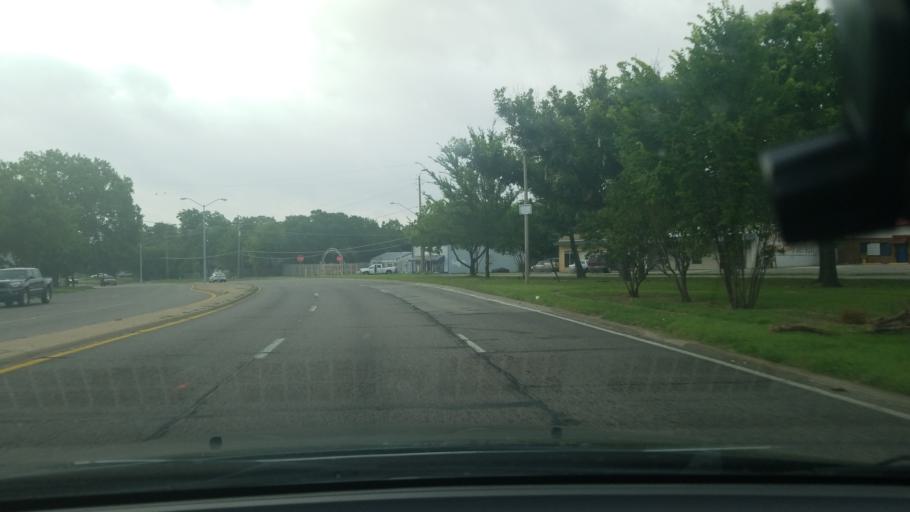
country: US
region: Texas
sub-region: Dallas County
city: Balch Springs
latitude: 32.7638
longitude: -96.6773
